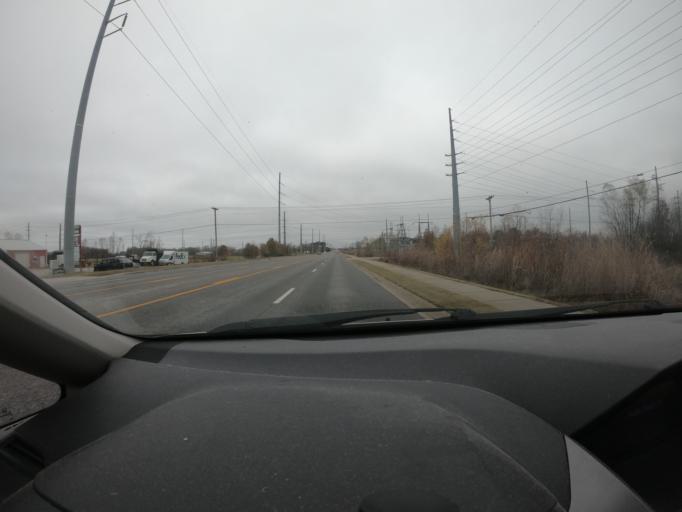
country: US
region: Arkansas
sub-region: Benton County
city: Bentonville
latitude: 36.3577
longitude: -94.2434
